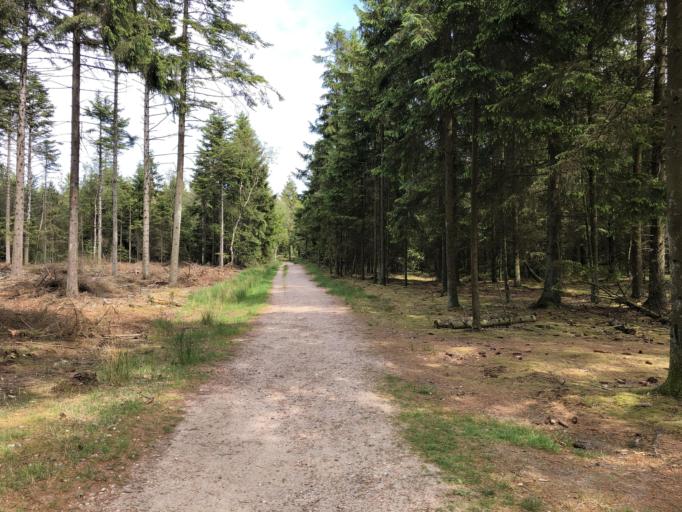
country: DK
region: Central Jutland
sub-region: Holstebro Kommune
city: Holstebro
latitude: 56.3470
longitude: 8.5816
